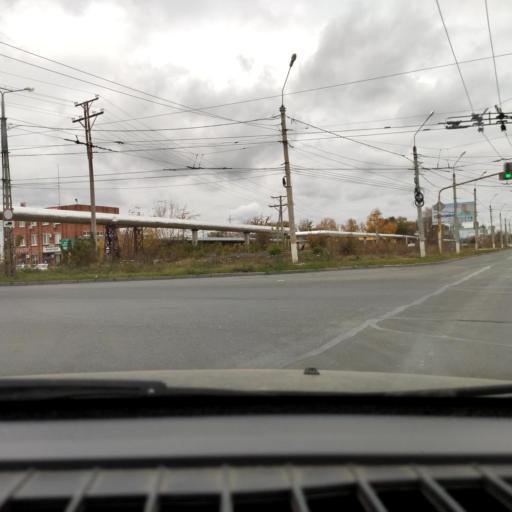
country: RU
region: Samara
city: Tol'yatti
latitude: 53.5329
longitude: 49.4391
